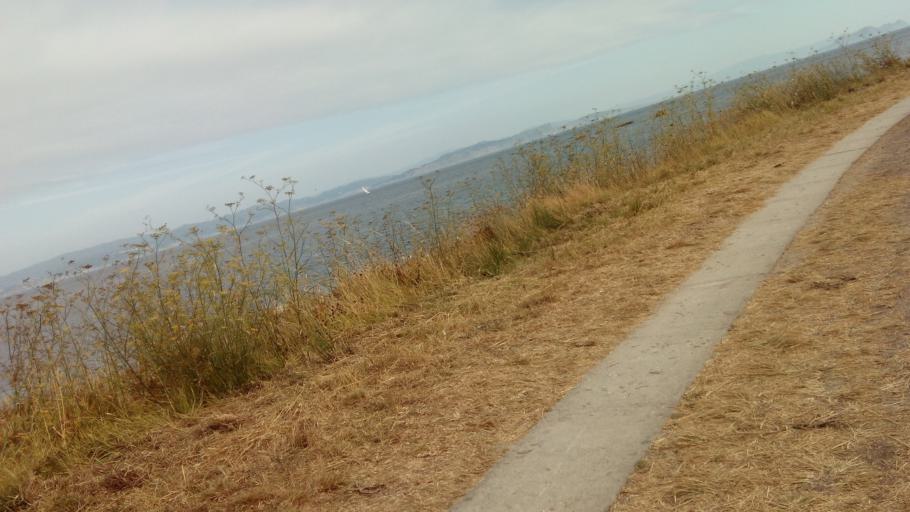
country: ES
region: Galicia
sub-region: Provincia de Pontevedra
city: Sanxenxo
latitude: 42.3729
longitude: -8.9327
